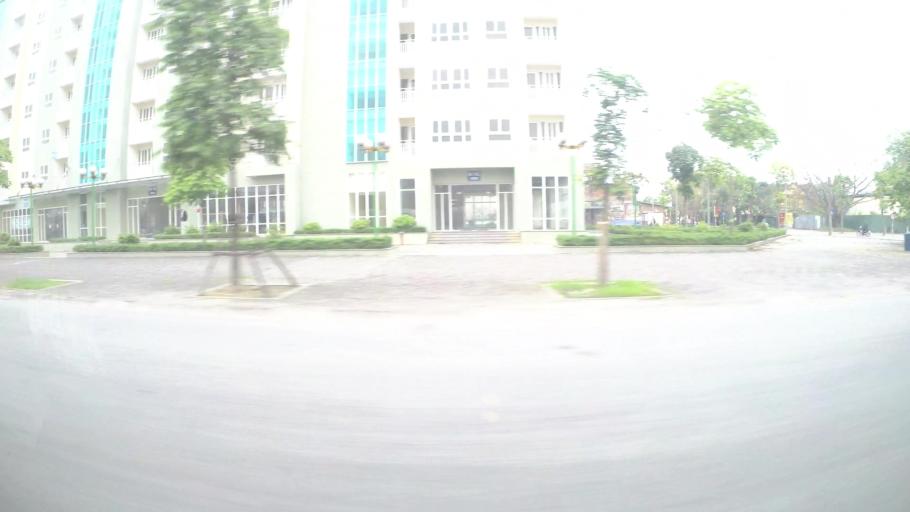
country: VN
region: Ha Noi
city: Hoan Kiem
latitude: 21.0600
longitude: 105.8834
